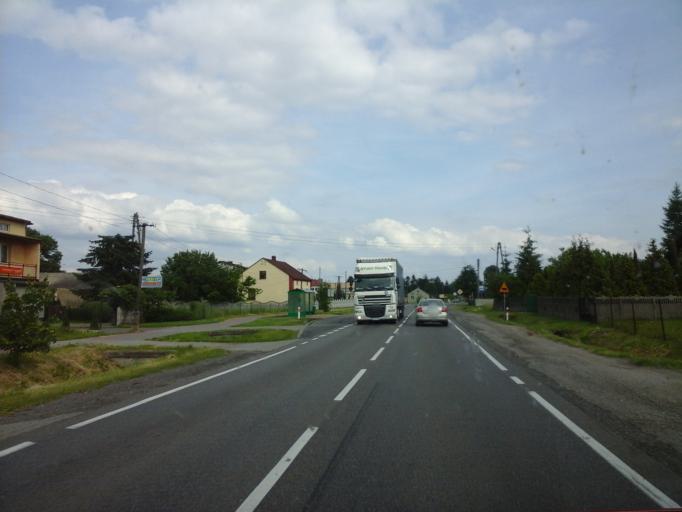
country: PL
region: Lodz Voivodeship
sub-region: Powiat opoczynski
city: Mniszkow
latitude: 51.3295
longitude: 20.0346
